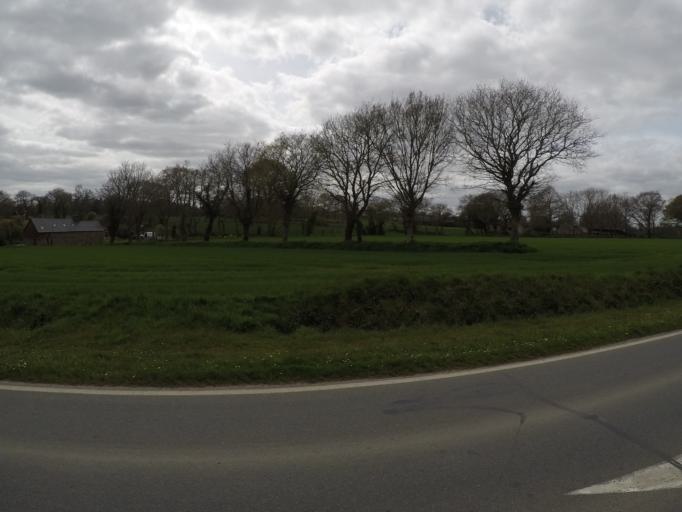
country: FR
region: Brittany
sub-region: Departement des Cotes-d'Armor
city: Plouha
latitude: 48.6693
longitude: -2.9282
